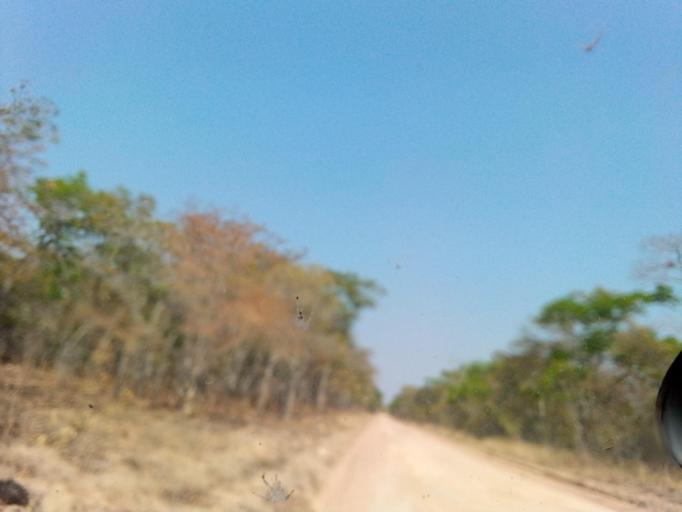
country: ZM
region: Northern
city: Mpika
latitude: -12.2422
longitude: 30.8424
